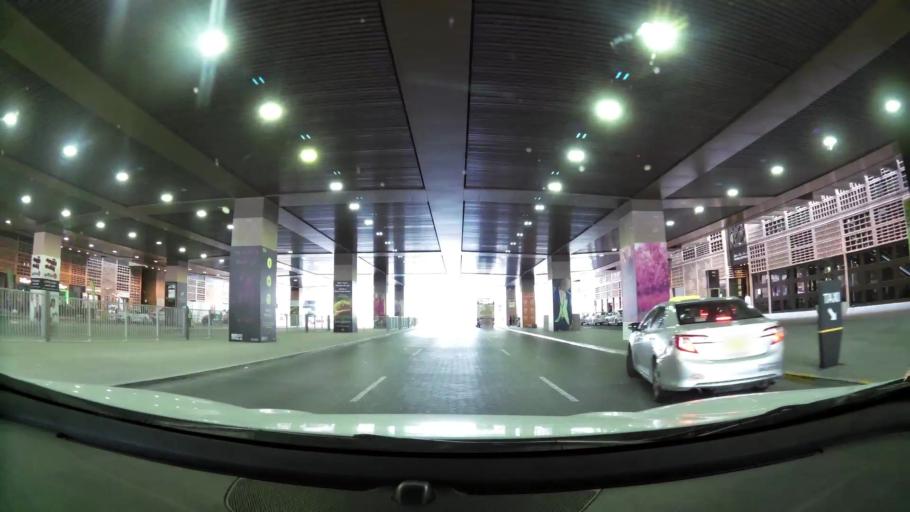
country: AE
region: Abu Dhabi
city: Abu Dhabi
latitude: 24.4885
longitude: 54.3564
